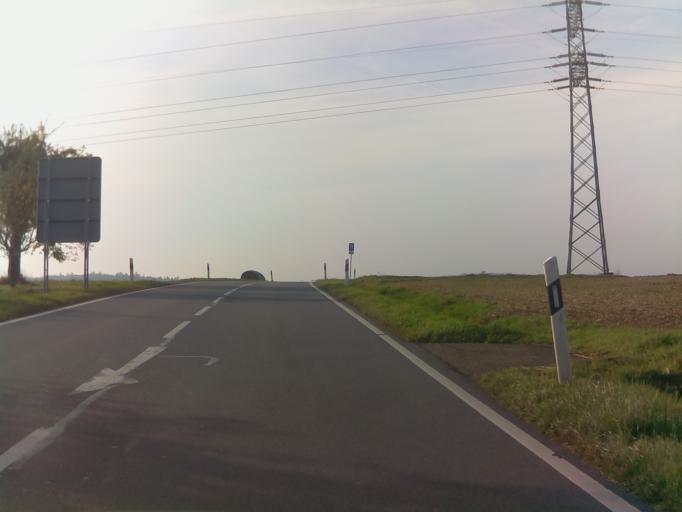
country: DE
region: Baden-Wuerttemberg
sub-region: Karlsruhe Region
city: Adelsheim
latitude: 49.4063
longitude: 9.3690
